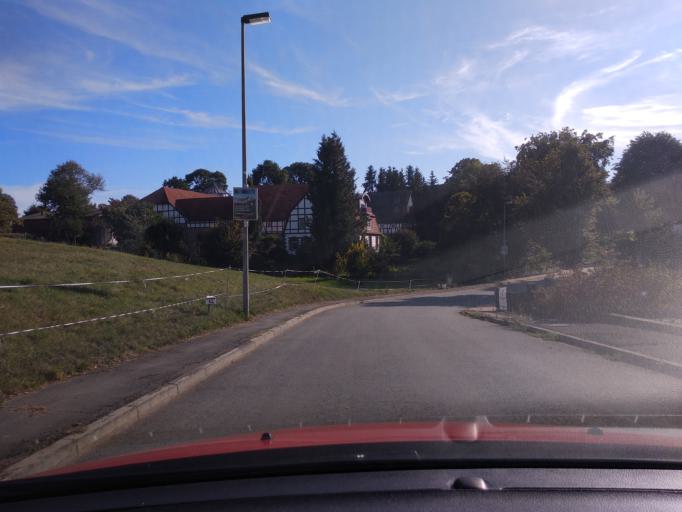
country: DE
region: North Rhine-Westphalia
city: Brakel
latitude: 51.6555
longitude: 9.1952
